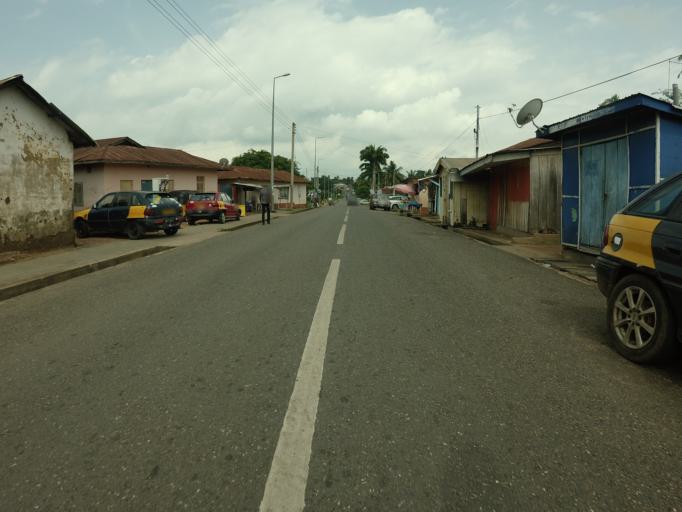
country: GH
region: Volta
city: Ho
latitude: 6.6141
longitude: 0.4712
